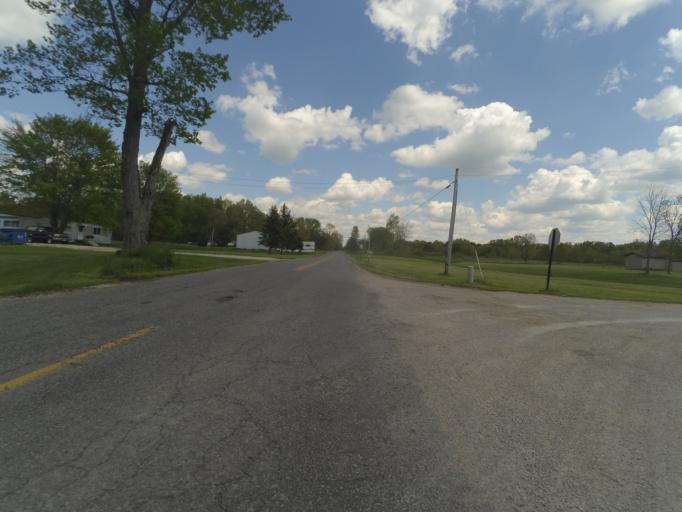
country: US
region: Ohio
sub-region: Mahoning County
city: Craig Beach
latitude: 41.1341
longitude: -81.0180
